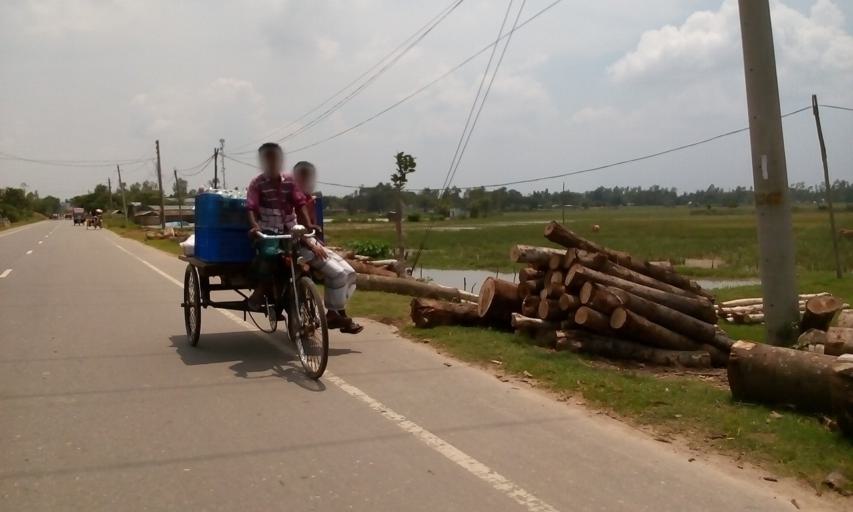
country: BD
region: Rangpur Division
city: Parbatipur
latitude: 25.5038
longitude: 88.9726
